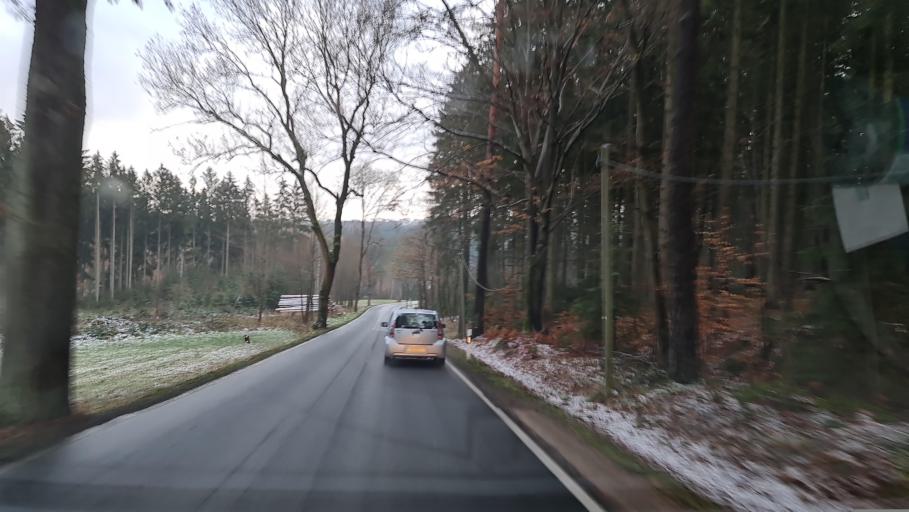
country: DE
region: Saxony
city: Mylau
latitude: 50.5940
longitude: 12.2807
